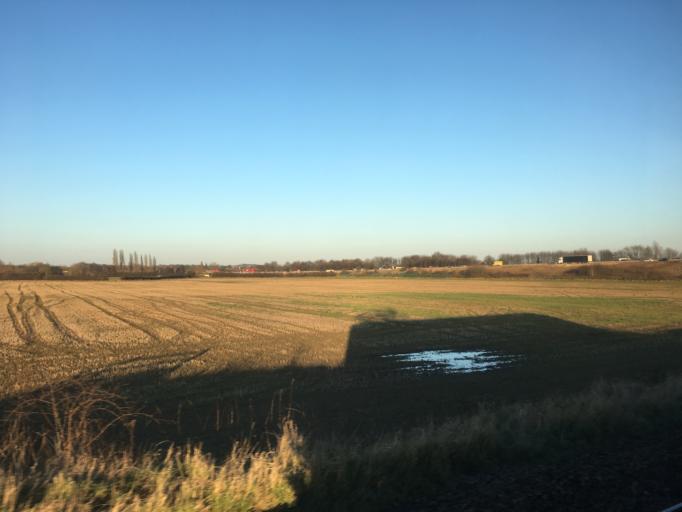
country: GB
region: England
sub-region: Derbyshire
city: Long Eaton
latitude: 52.8893
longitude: -1.3081
